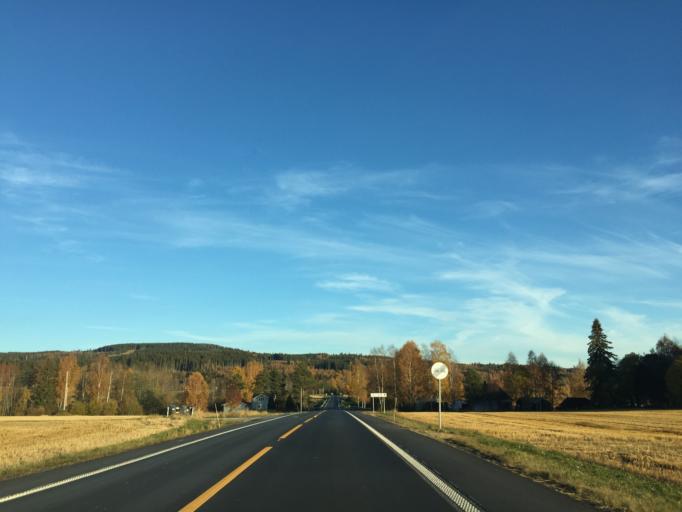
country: NO
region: Hedmark
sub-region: Kongsvinger
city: Spetalen
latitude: 60.2307
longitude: 11.8341
